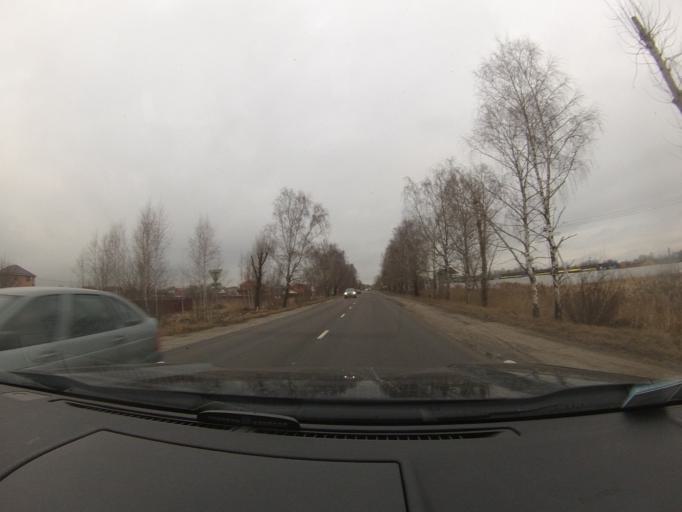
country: RU
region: Moskovskaya
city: Lopatinskiy
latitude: 55.3301
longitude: 38.7230
